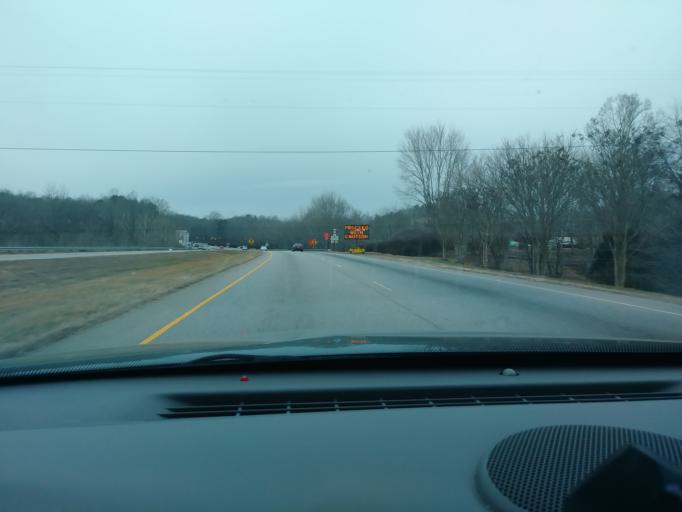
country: US
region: North Carolina
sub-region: Wilkes County
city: Wilkesboro
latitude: 36.1485
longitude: -81.1815
